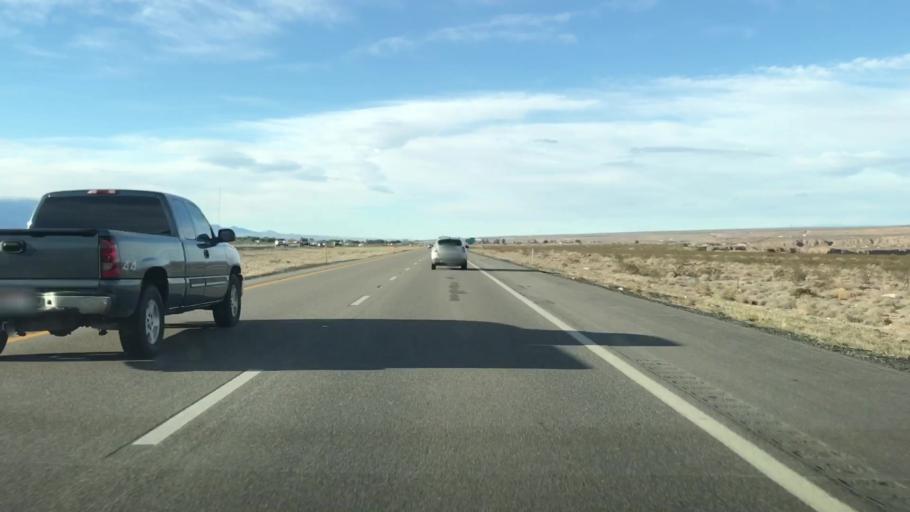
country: US
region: Arizona
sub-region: Mohave County
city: Beaver Dam
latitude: 36.9117
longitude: -113.8847
